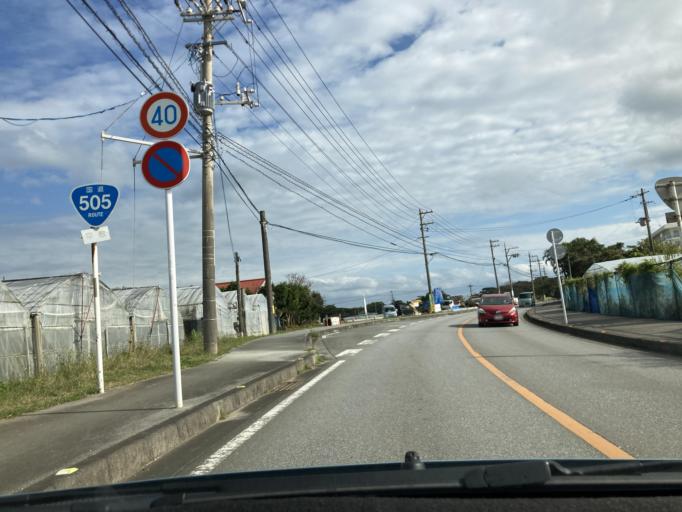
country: JP
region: Okinawa
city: Nago
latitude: 26.6905
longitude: 127.9630
